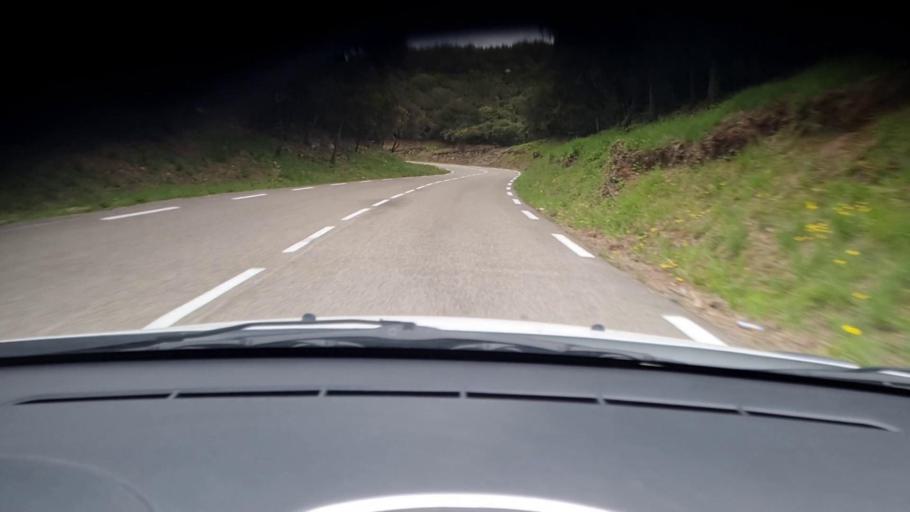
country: FR
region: Languedoc-Roussillon
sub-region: Departement du Gard
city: Poulx
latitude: 43.9268
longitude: 4.3915
